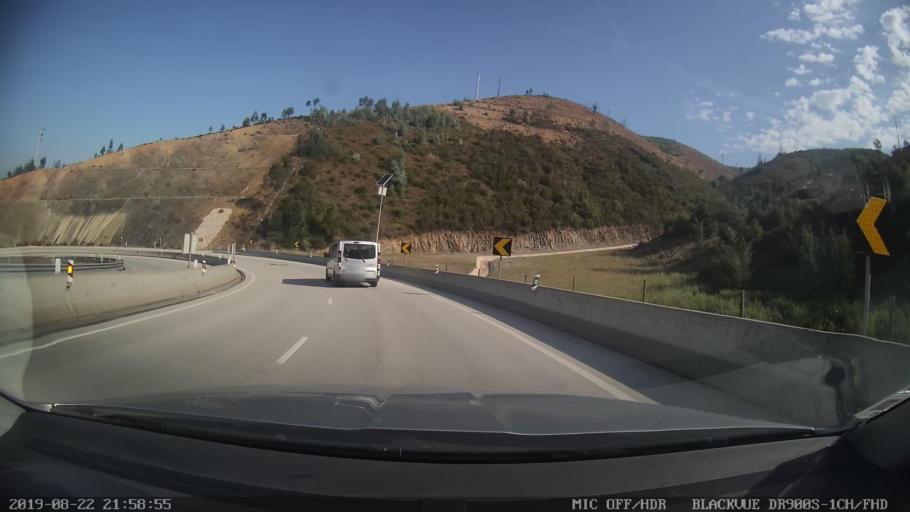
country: PT
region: Coimbra
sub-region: Coimbra
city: Coimbra
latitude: 40.1807
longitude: -8.3893
